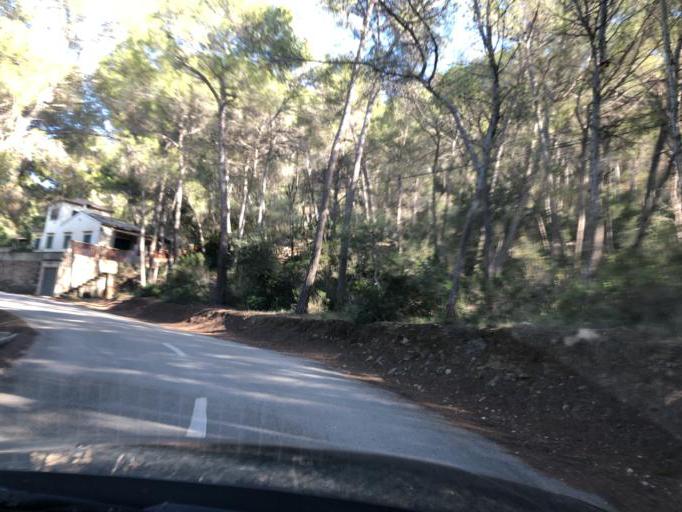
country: ES
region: Balearic Islands
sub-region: Illes Balears
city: Camp de Mar
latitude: 39.5415
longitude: 2.3978
